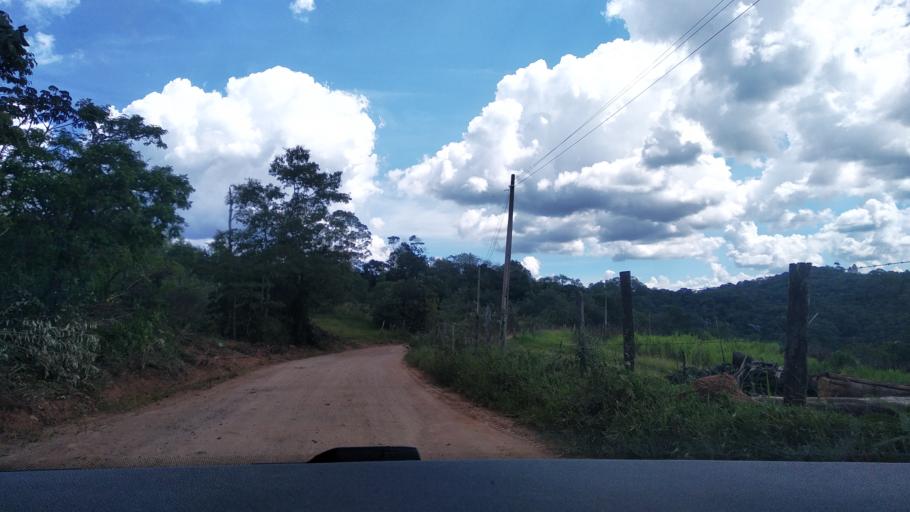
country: BR
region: Sao Paulo
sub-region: Cajamar
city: Cajamar
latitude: -23.2841
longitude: -46.8881
